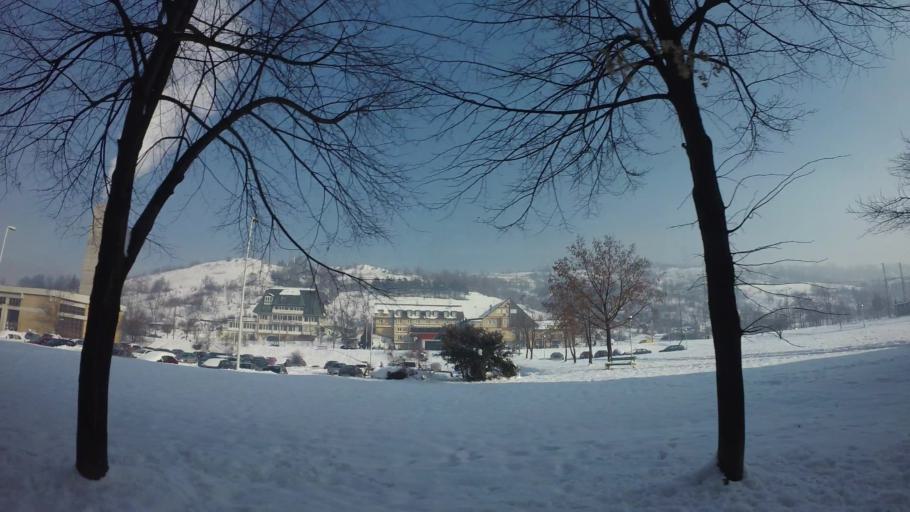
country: BA
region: Federation of Bosnia and Herzegovina
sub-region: Kanton Sarajevo
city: Sarajevo
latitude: 43.8321
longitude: 18.3473
